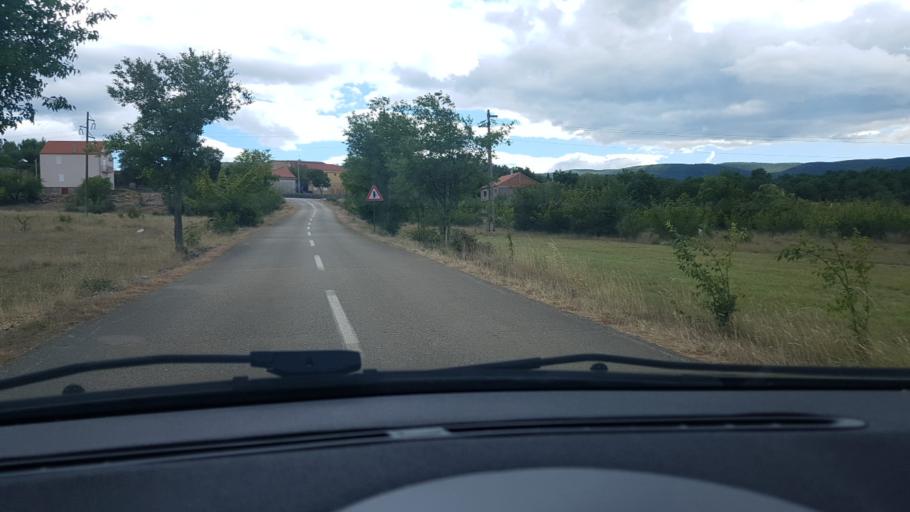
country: HR
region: Zadarska
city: Gracac
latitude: 44.1585
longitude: 15.8568
